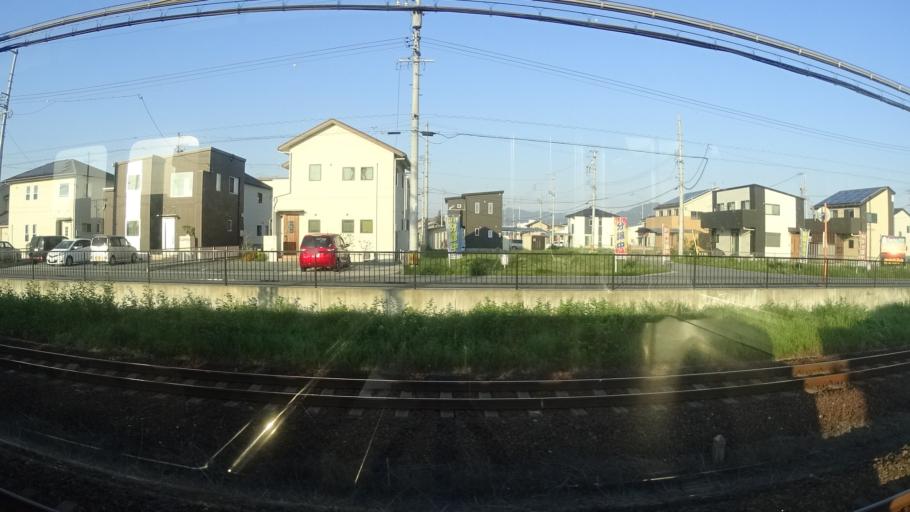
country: JP
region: Mie
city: Hisai-motomachi
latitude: 34.5695
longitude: 136.5425
